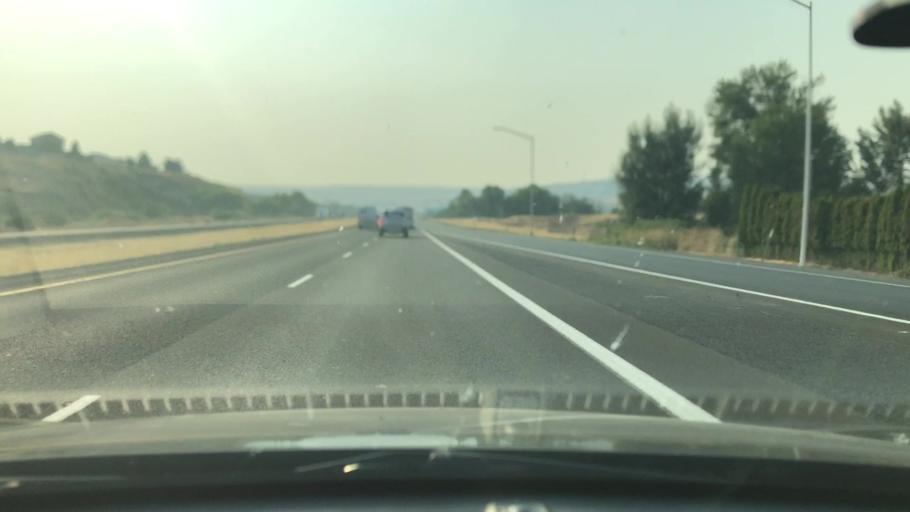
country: US
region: Oregon
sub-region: Umatilla County
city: Pendleton
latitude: 45.6649
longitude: -118.8115
